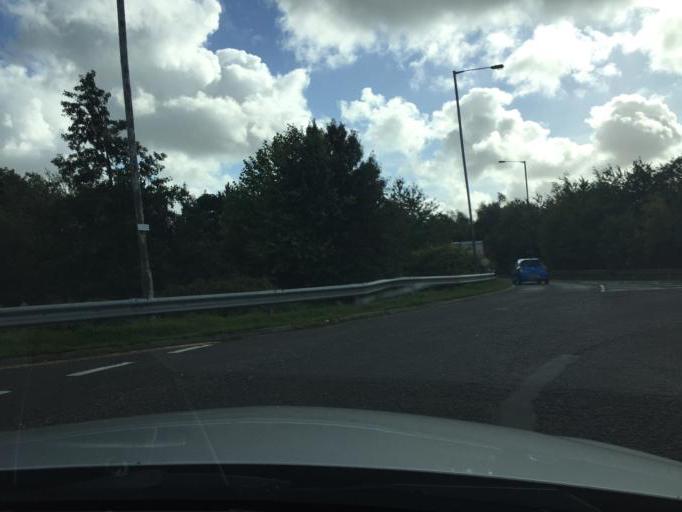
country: GB
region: England
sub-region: Lancashire
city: Kirkham
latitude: 53.7856
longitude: -2.8934
